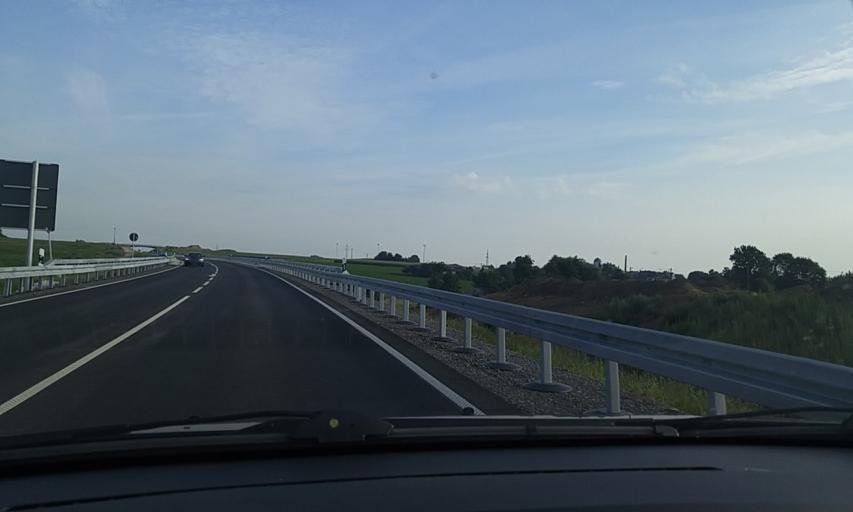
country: DE
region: Hesse
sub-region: Regierungsbezirk Darmstadt
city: Karben
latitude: 50.2723
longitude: 8.7604
